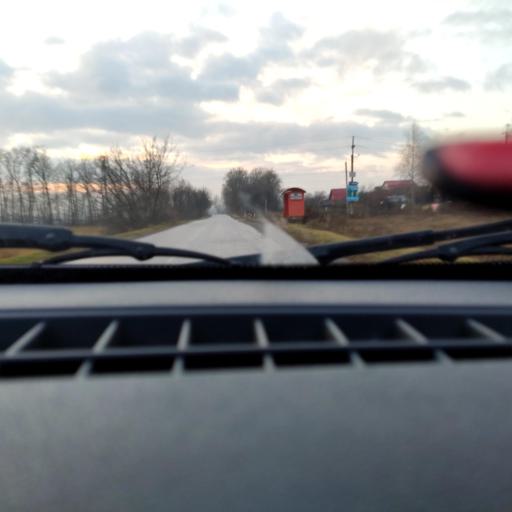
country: RU
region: Bashkortostan
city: Avdon
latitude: 54.5093
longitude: 55.8334
